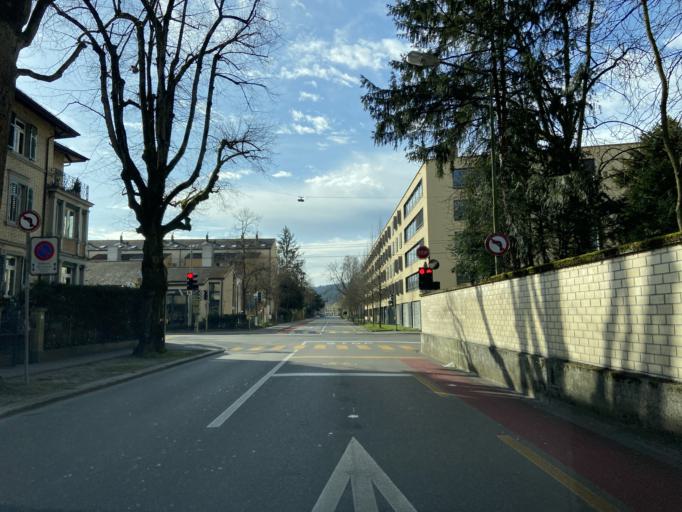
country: CH
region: Zurich
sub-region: Bezirk Winterthur
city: Mattenbach (Kreis 7) / Deutweg
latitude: 47.4986
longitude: 8.7397
